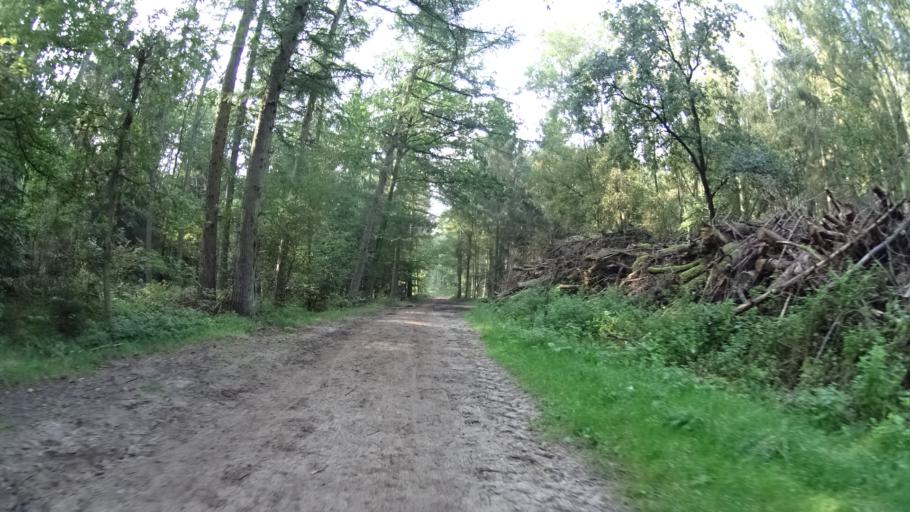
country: DE
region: Lower Saxony
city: Reppenstedt
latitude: 53.2289
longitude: 10.3465
